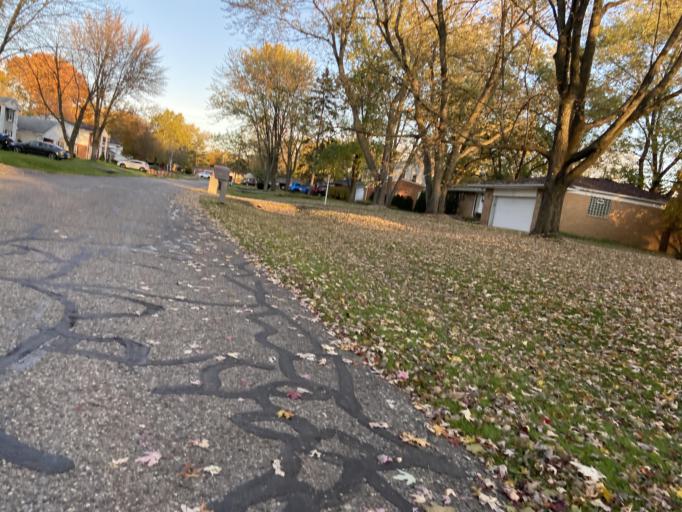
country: US
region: Michigan
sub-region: Oakland County
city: Farmington Hills
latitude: 42.5027
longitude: -83.3685
